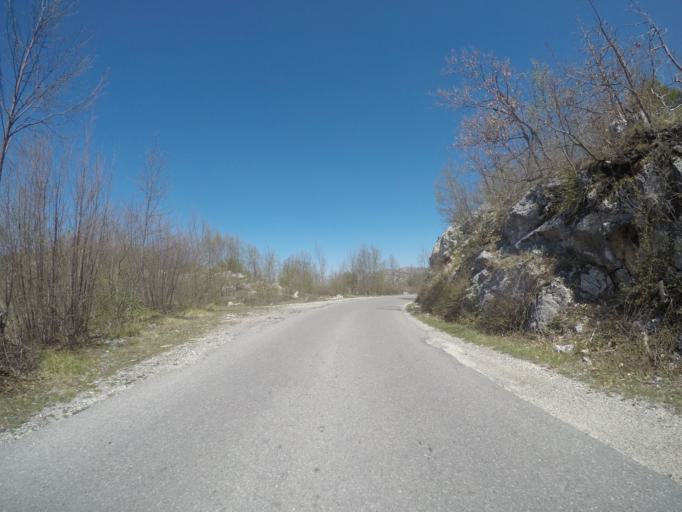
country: ME
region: Cetinje
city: Cetinje
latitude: 42.4458
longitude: 18.8733
